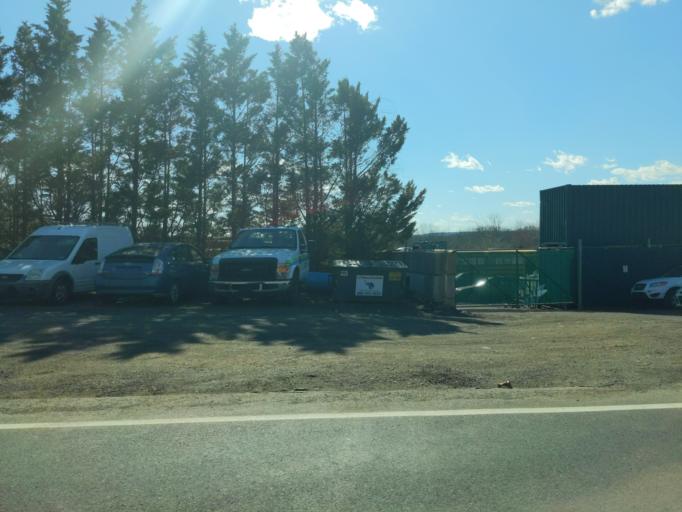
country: US
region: Pennsylvania
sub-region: Montgomery County
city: Red Hill
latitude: 40.3794
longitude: -75.4611
